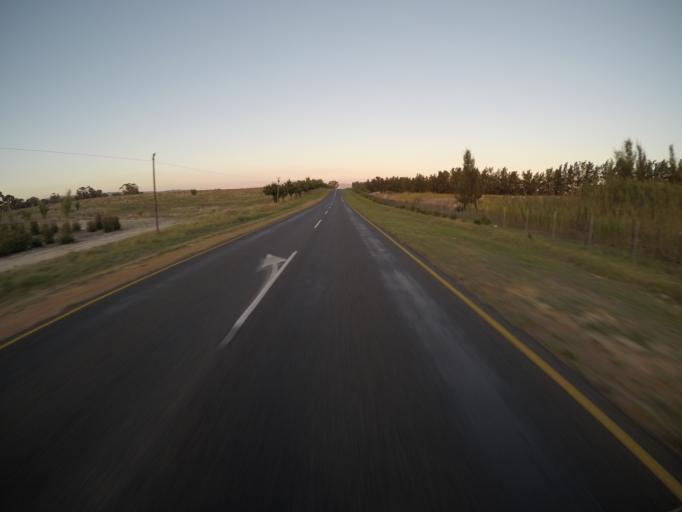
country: ZA
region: Western Cape
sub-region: Cape Winelands District Municipality
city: Paarl
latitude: -33.8056
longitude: 18.8817
